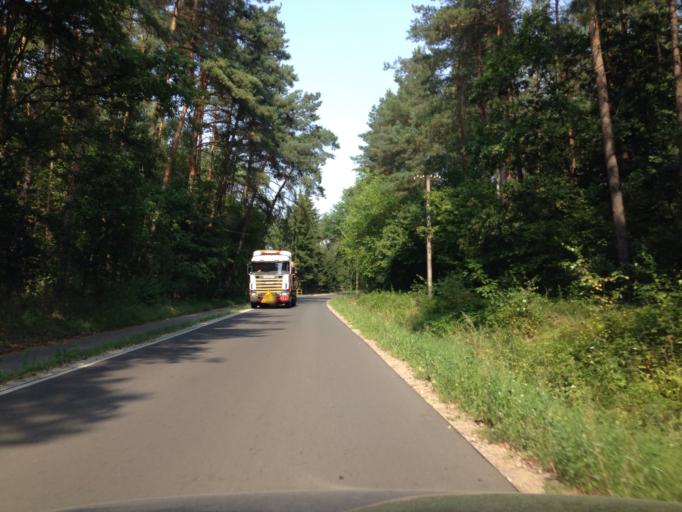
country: PL
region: Kujawsko-Pomorskie
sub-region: Powiat golubsko-dobrzynski
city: Golub-Dobrzyn
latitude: 53.0798
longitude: 19.0309
